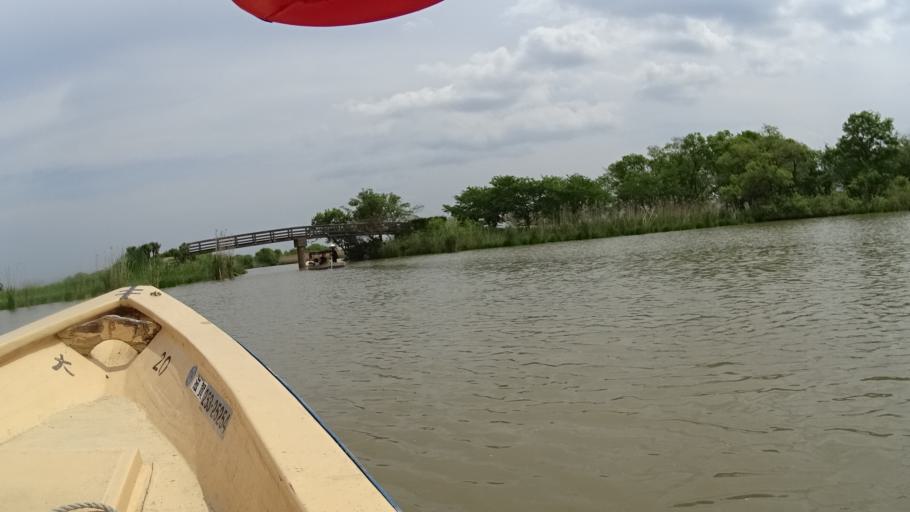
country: JP
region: Shiga Prefecture
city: Omihachiman
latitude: 35.1556
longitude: 136.1006
